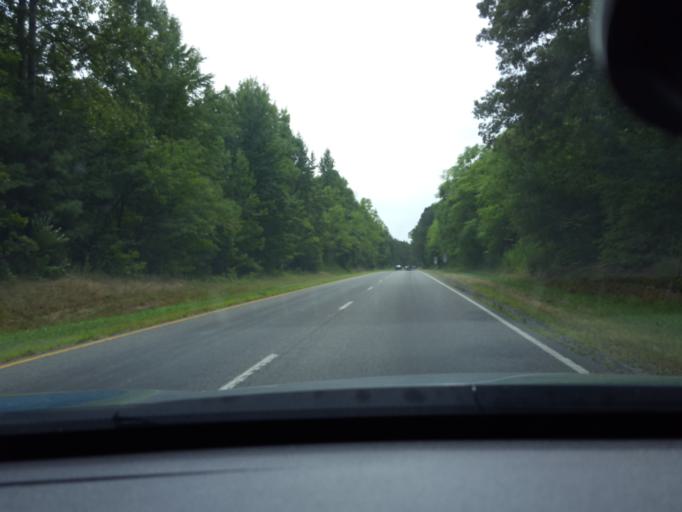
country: US
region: Virginia
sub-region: Caroline County
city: Bowling Green
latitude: 38.1276
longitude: -77.2427
